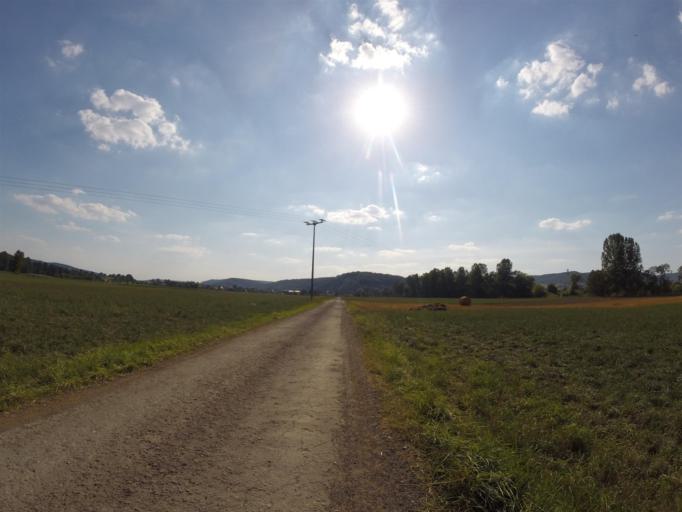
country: DE
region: Thuringia
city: Sulza
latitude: 50.8504
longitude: 11.6172
